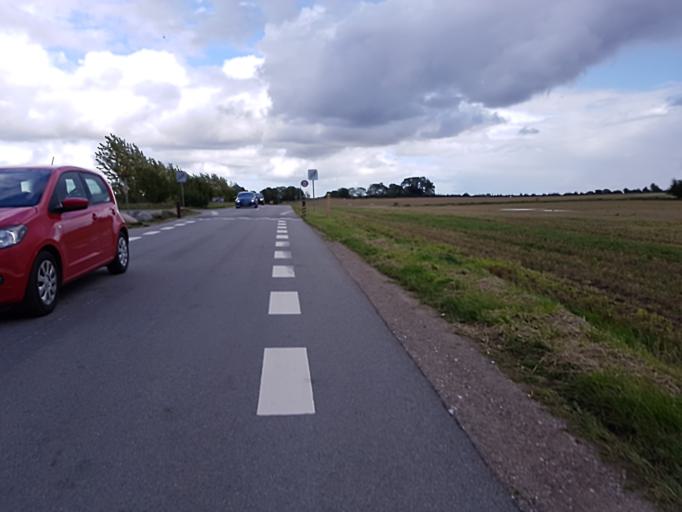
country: DK
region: Zealand
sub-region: Roskilde Kommune
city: Gundsomagle
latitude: 55.7150
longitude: 12.1422
